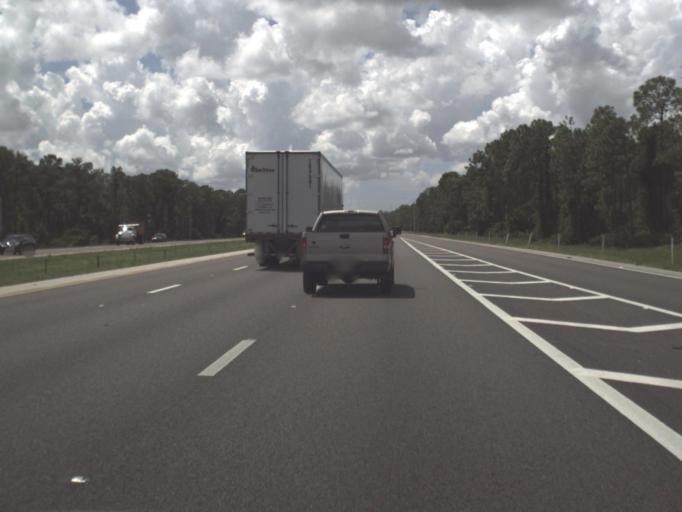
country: US
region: Florida
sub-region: Collier County
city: Vineyards
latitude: 26.2690
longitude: -81.7429
